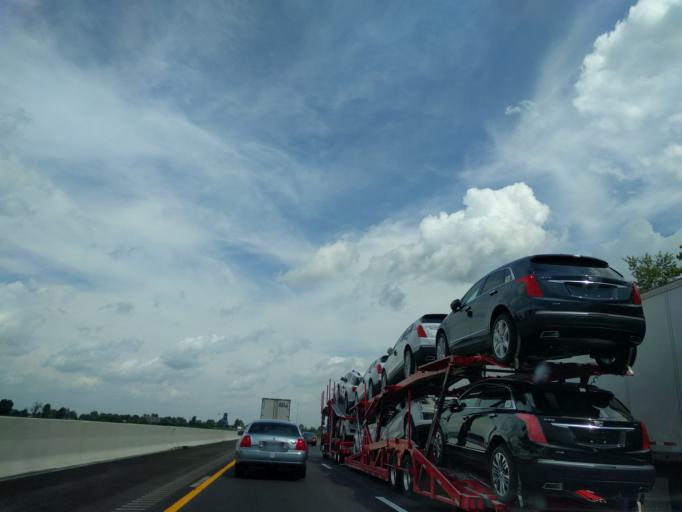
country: US
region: Kentucky
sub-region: Larue County
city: Hodgenville
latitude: 37.5104
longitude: -85.8873
